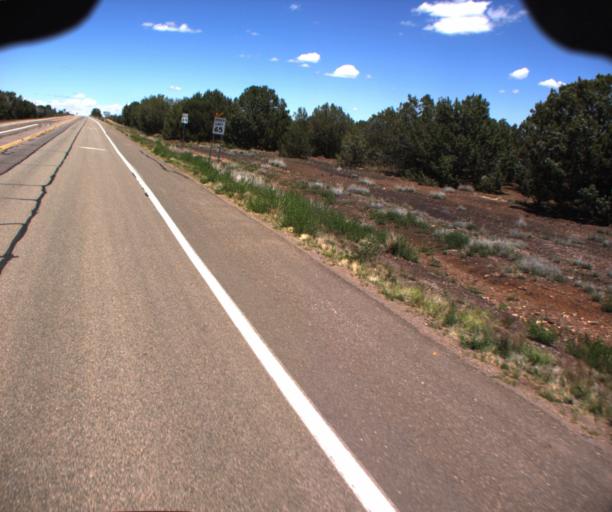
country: US
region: Arizona
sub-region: Yavapai County
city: Paulden
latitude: 35.0047
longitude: -112.3897
